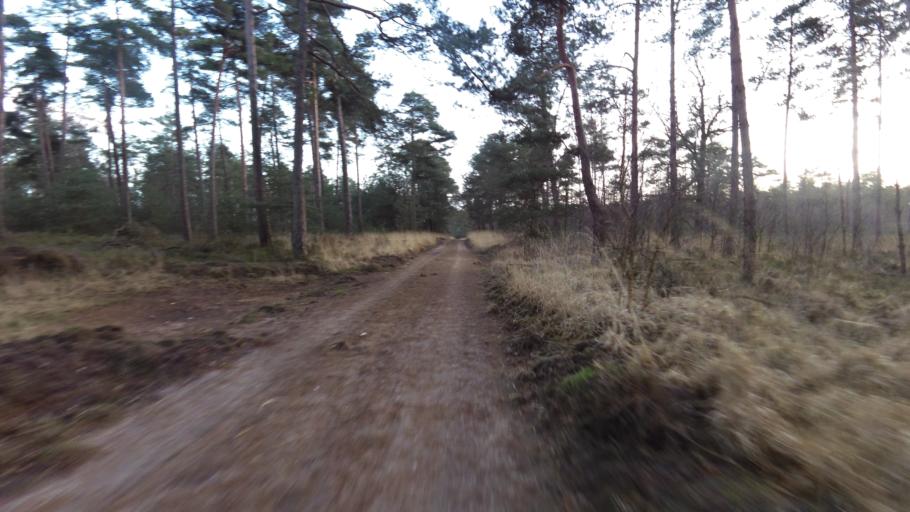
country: NL
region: Gelderland
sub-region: Gemeente Apeldoorn
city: Uddel
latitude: 52.2920
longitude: 5.8508
